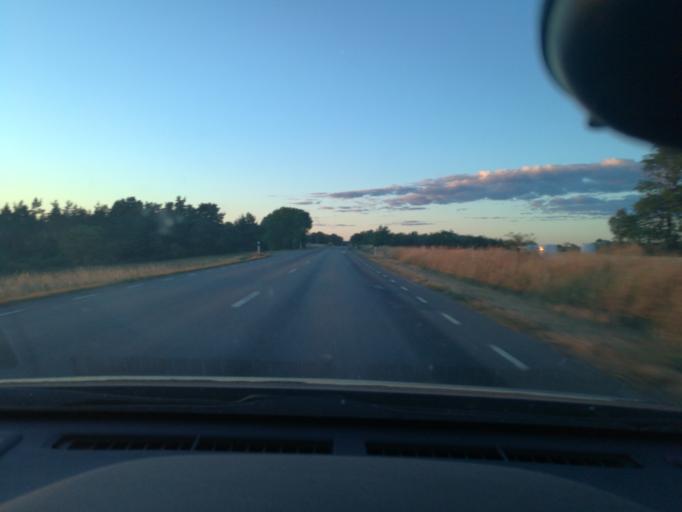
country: SE
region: Kalmar
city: Faerjestaden
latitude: 56.7097
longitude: 16.5295
